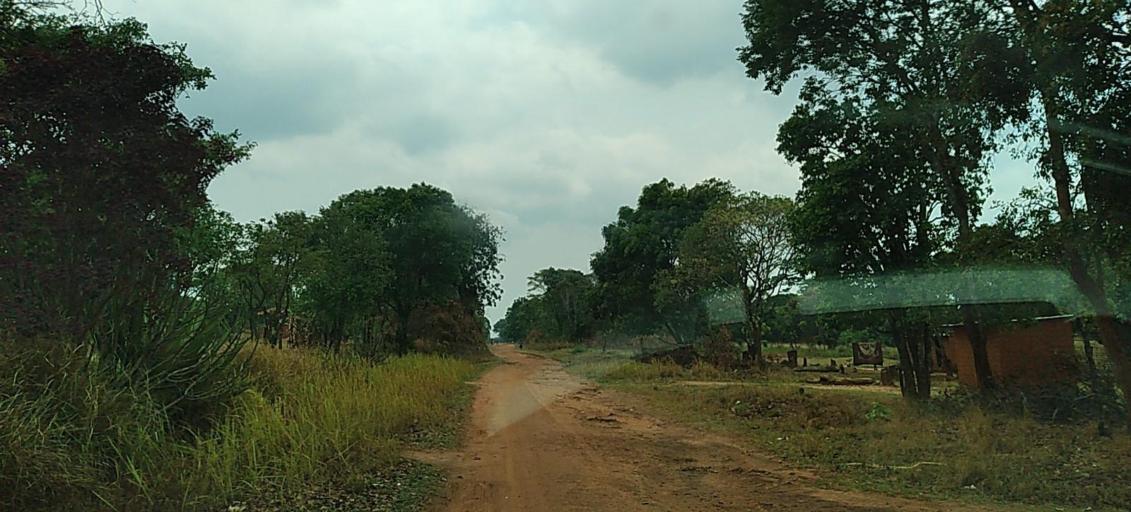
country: ZM
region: North-Western
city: Mwinilunga
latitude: -11.5298
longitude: 24.7853
